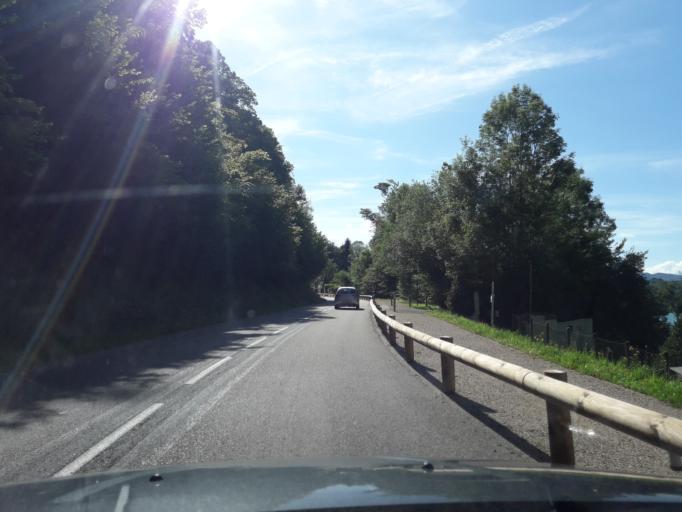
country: FR
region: Rhone-Alpes
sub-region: Departement de la Savoie
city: Vimines
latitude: 45.5588
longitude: 5.8116
